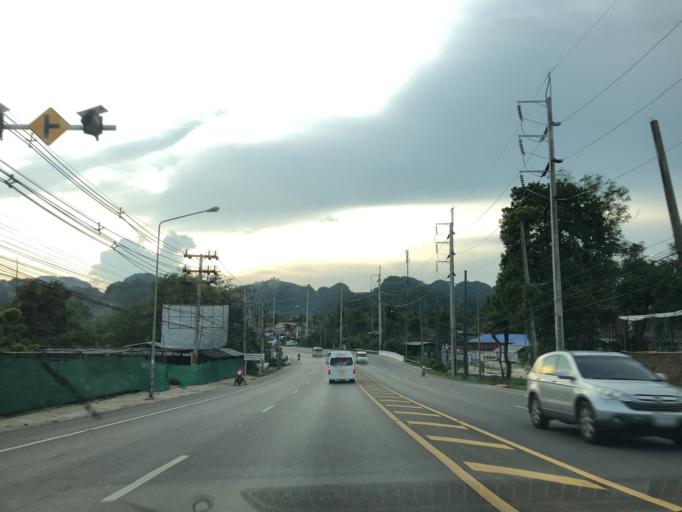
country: TH
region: Krabi
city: Krabi
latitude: 8.0840
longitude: 98.8879
